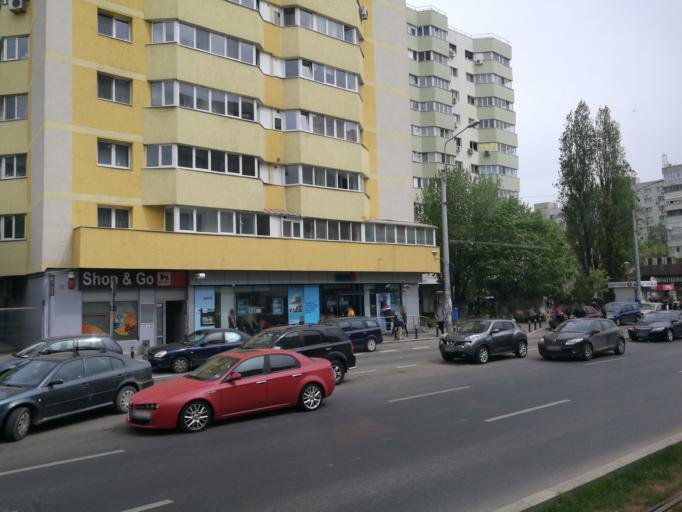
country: RO
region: Ilfov
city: Dobroesti
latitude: 44.4412
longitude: 26.1808
